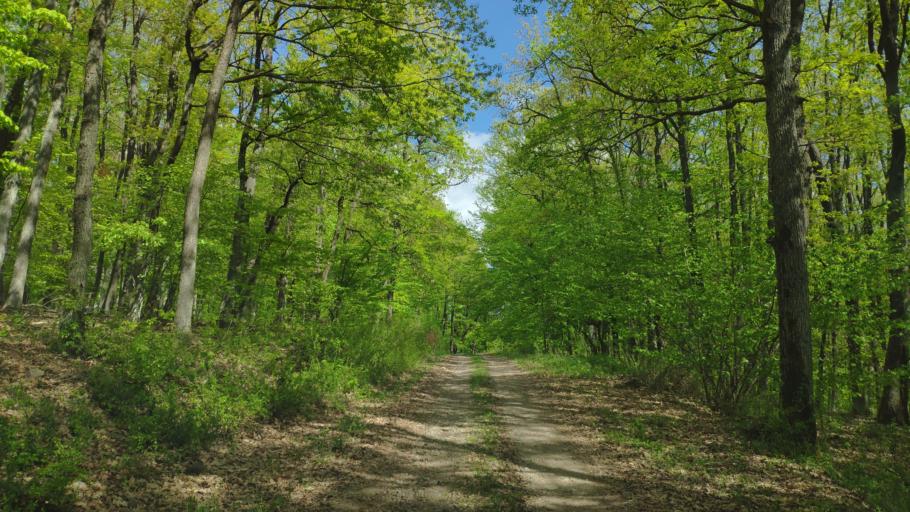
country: SK
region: Kosicky
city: Kosice
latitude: 48.6594
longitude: 21.4403
